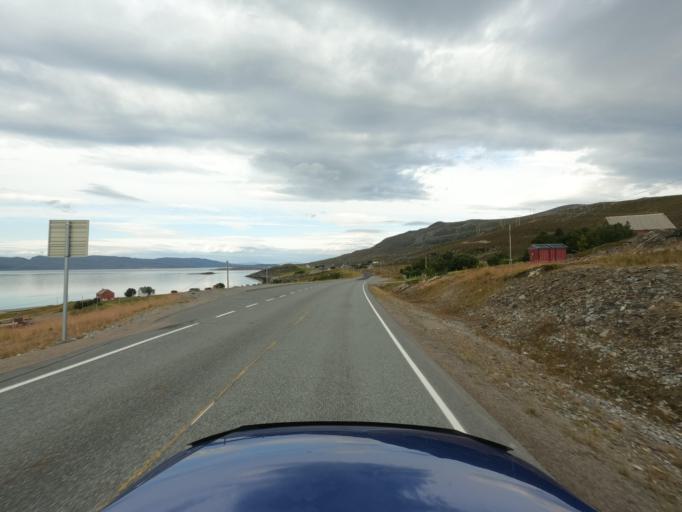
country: NO
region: Finnmark Fylke
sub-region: Hammerfest
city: Rypefjord
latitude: 70.5403
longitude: 23.7365
